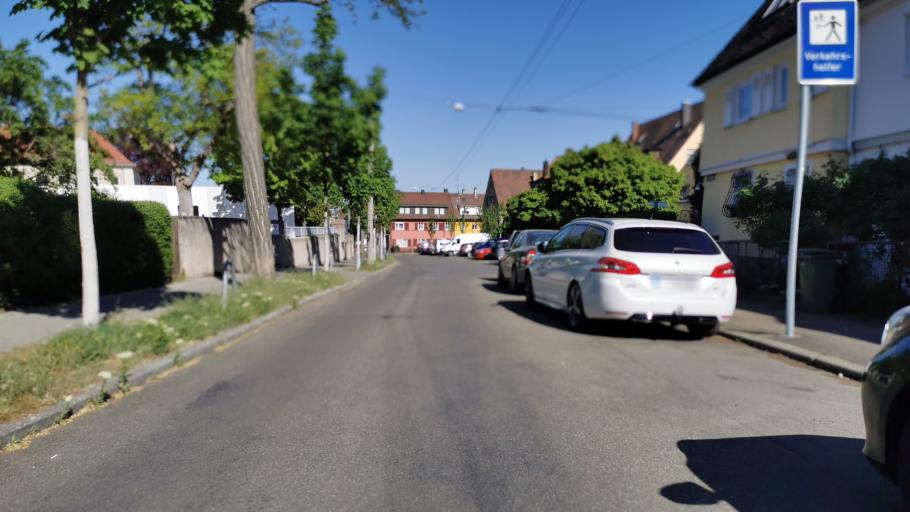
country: DE
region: Baden-Wuerttemberg
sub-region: Regierungsbezirk Stuttgart
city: Stuttgart-Ost
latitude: 48.8105
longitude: 9.2067
